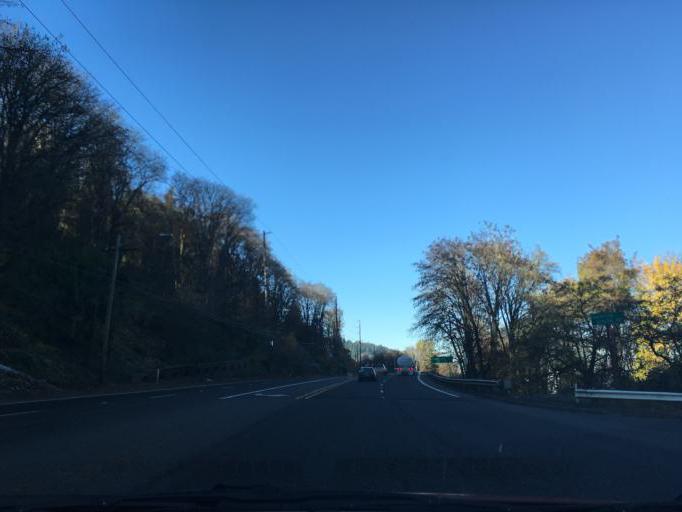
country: US
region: Oregon
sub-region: Washington County
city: West Haven
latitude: 45.5853
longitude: -122.7706
